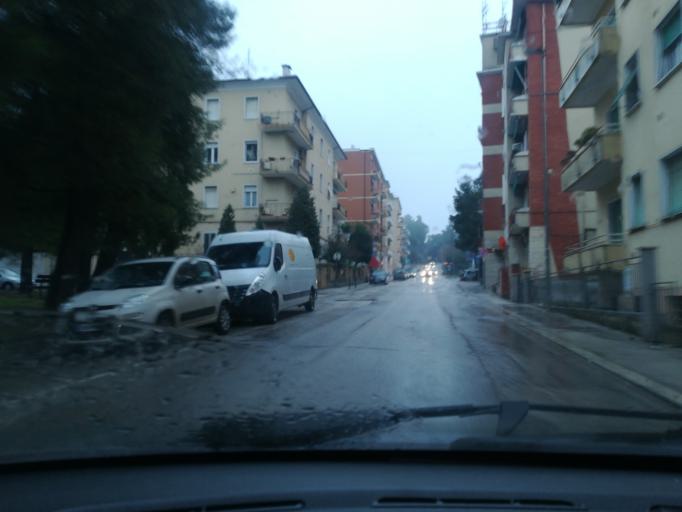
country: IT
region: The Marches
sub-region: Provincia di Macerata
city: Macerata
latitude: 43.2952
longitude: 13.4361
